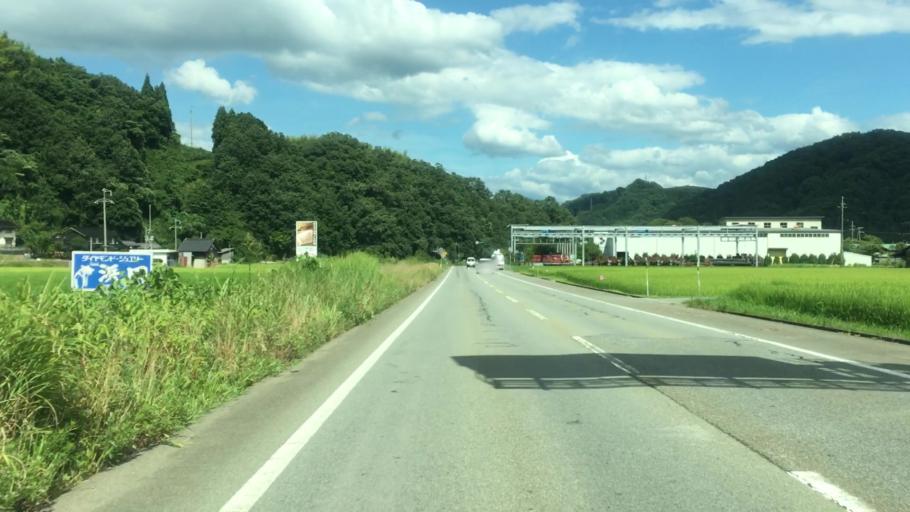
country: JP
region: Hyogo
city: Toyooka
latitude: 35.4653
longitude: 134.7511
